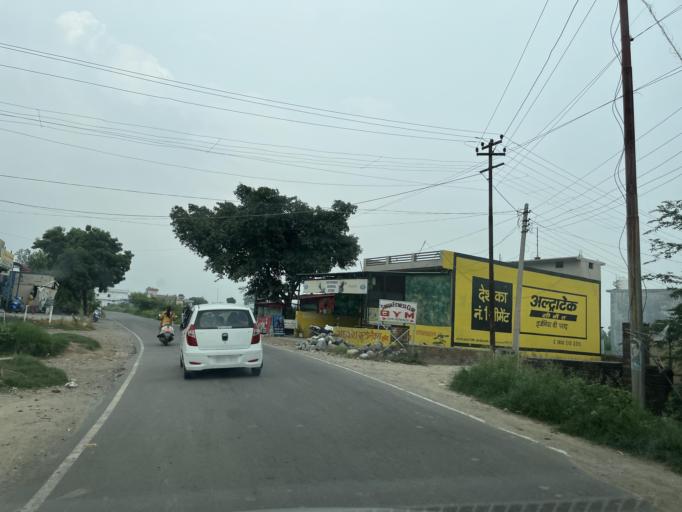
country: IN
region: Uttarakhand
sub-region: Naini Tal
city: Haldwani
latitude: 29.1927
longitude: 79.4822
